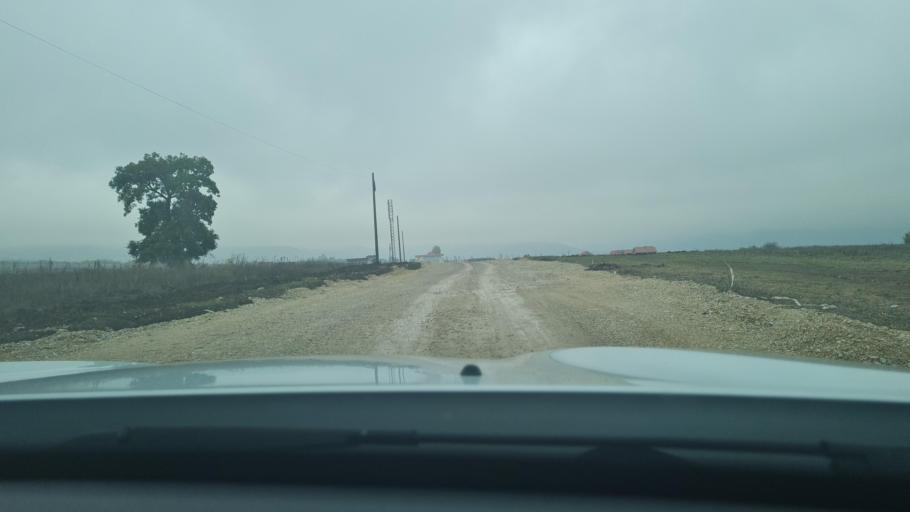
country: MK
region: Opstina Lipkovo
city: Matejche
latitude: 42.1142
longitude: 21.6102
